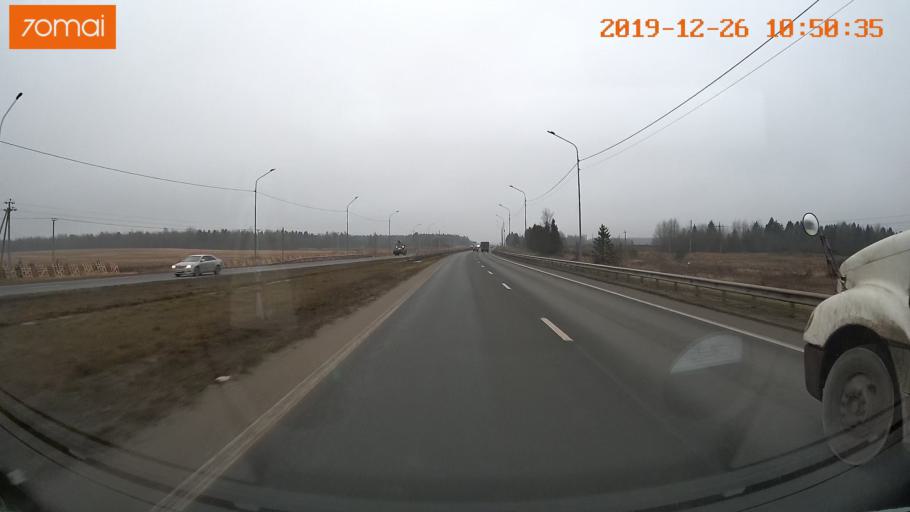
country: RU
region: Vologda
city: Molochnoye
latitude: 59.2081
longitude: 39.6849
